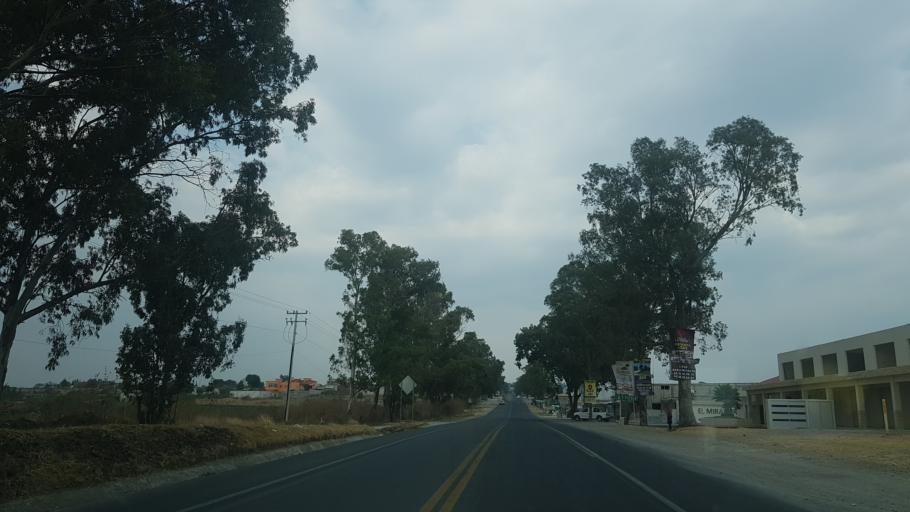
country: MX
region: Puebla
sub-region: Santa Isabel Cholula
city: San Pablo Ahuatempa
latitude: 18.9763
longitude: -98.3730
